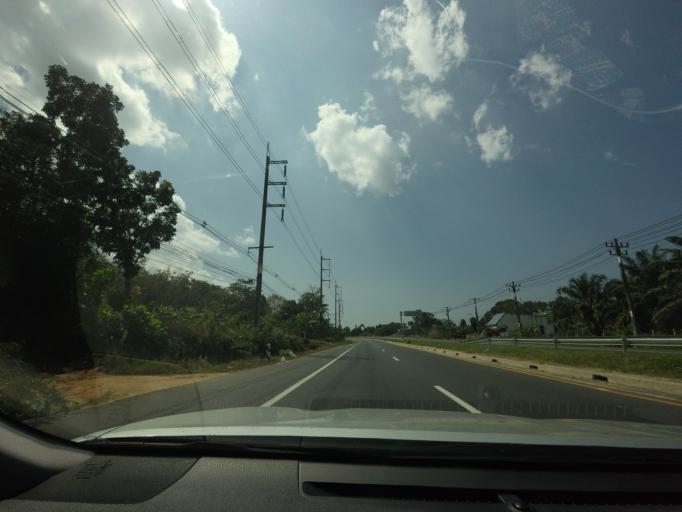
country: TH
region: Phangnga
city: Thai Mueang
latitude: 8.4189
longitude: 98.2590
